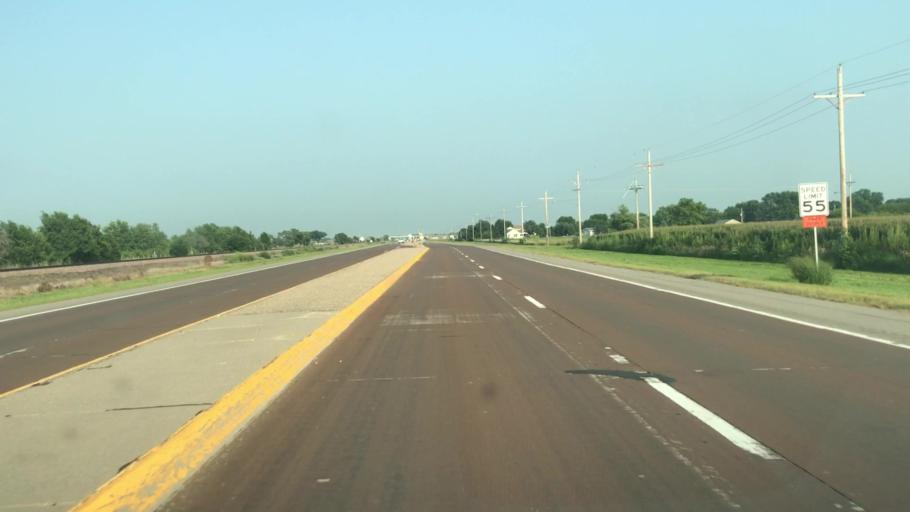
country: US
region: Nebraska
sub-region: Hall County
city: Grand Island
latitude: 40.9590
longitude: -98.4092
